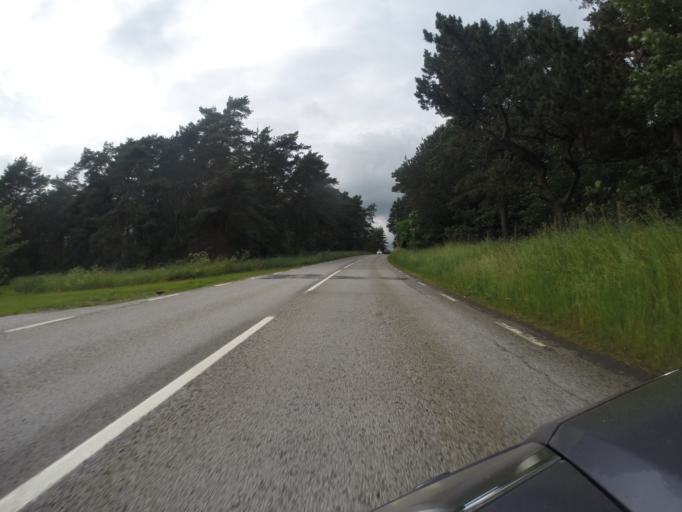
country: SE
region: Skane
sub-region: Kavlinge Kommun
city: Hofterup
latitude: 55.8318
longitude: 12.9628
